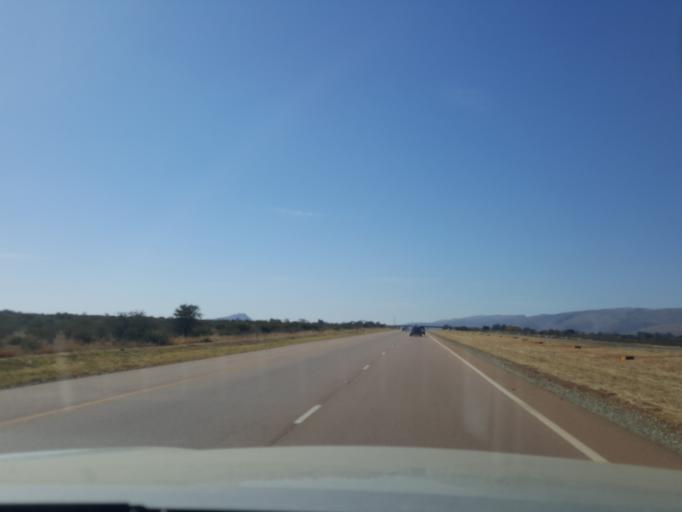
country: ZA
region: North-West
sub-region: Bojanala Platinum District Municipality
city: Brits
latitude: -25.7369
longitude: 27.6234
